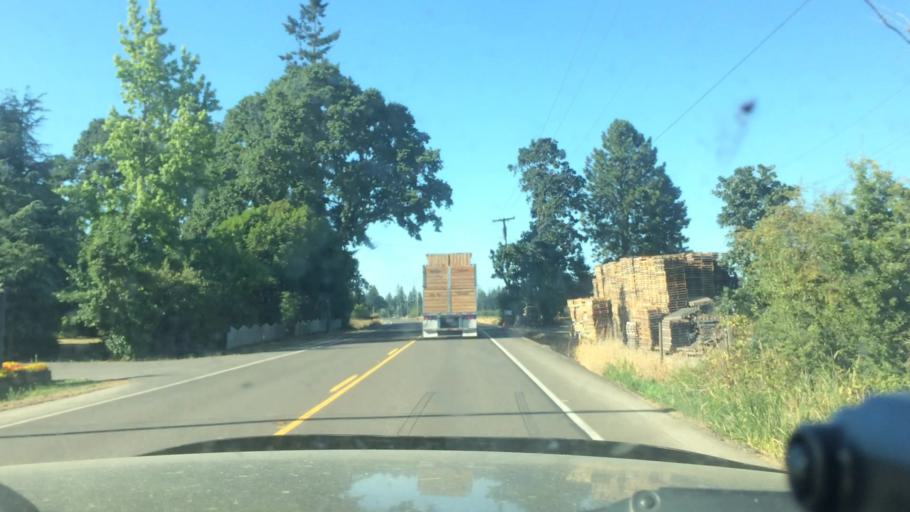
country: US
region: Oregon
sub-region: Marion County
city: Hayesville
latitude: 45.0619
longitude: -122.9815
